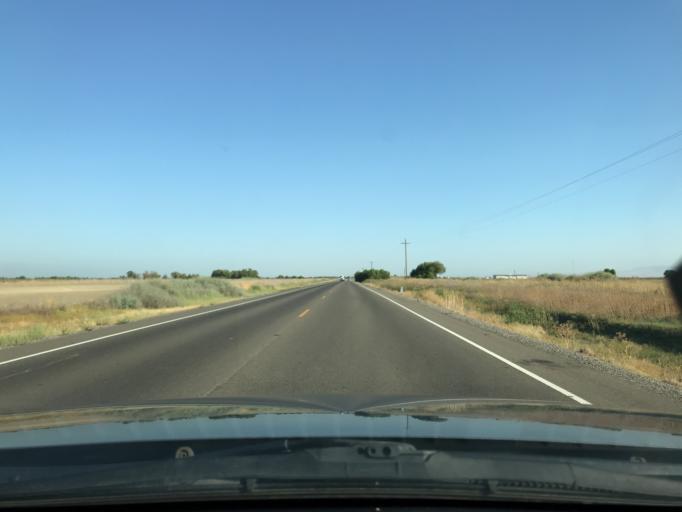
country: US
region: California
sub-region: Merced County
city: Los Banos
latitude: 37.1988
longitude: -120.8423
